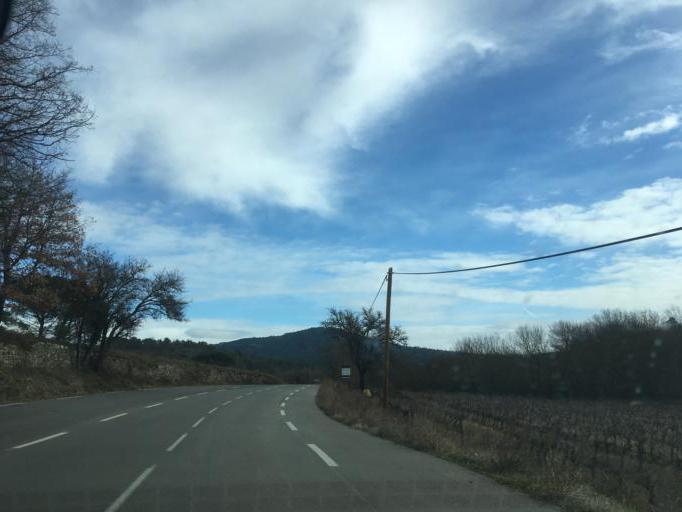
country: FR
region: Provence-Alpes-Cote d'Azur
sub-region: Departement du Var
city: Bras
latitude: 43.4637
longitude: 5.9406
